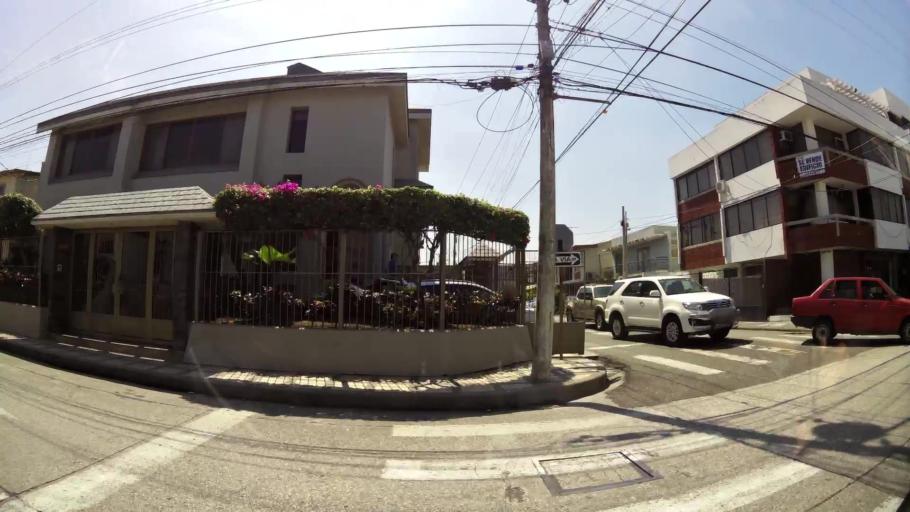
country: EC
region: Guayas
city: Guayaquil
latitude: -2.1681
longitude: -79.9114
